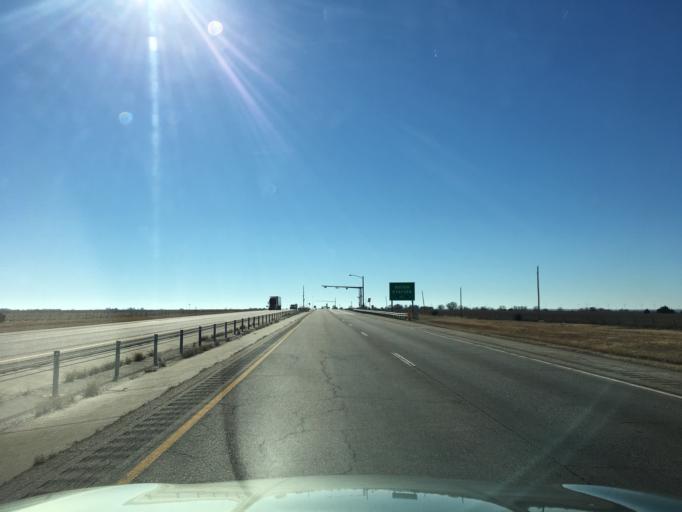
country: US
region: Oklahoma
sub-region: Kay County
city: Blackwell
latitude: 36.9988
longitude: -97.3428
